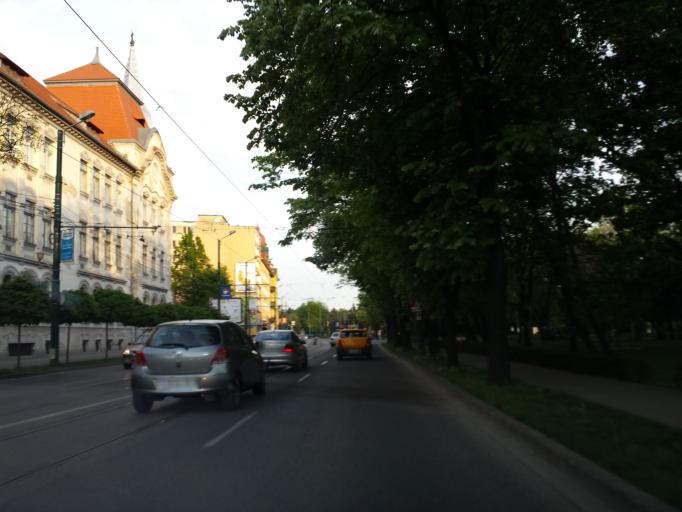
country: RO
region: Timis
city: Timisoara
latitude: 45.7524
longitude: 21.2218
